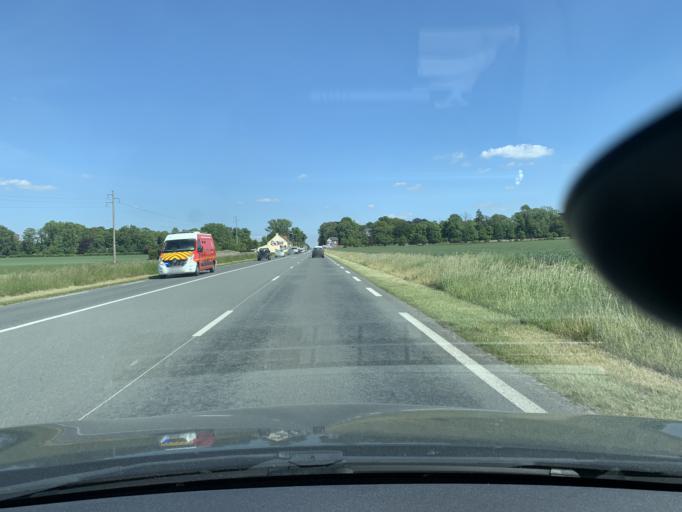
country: FR
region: Nord-Pas-de-Calais
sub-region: Departement du Nord
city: Fontaine-au-Pire
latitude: 50.1512
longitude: 3.3371
